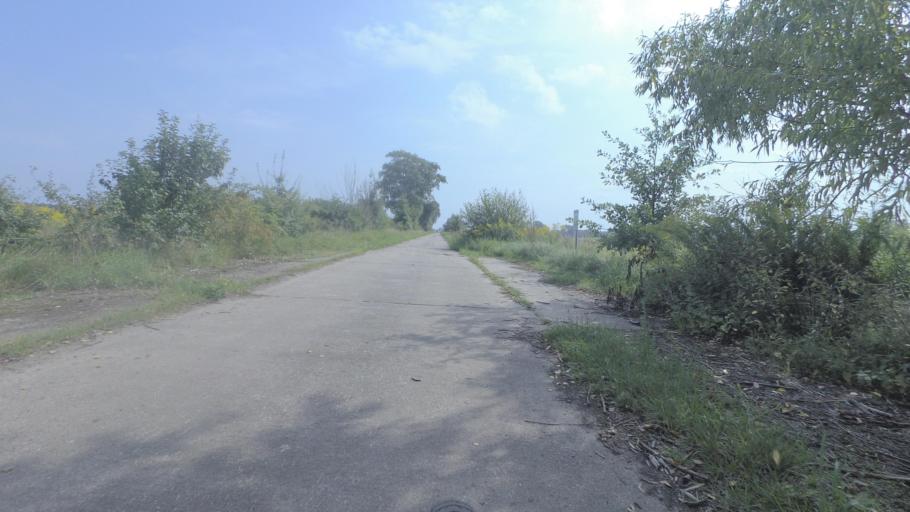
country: DE
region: Brandenburg
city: Mittenwalde
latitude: 52.2660
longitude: 13.4846
